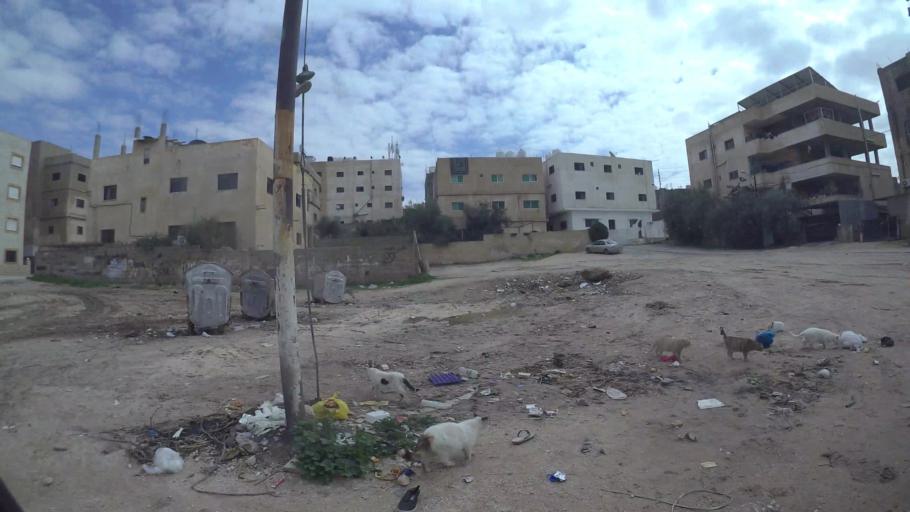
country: JO
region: Amman
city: Al Jubayhah
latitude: 32.0610
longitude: 35.8291
